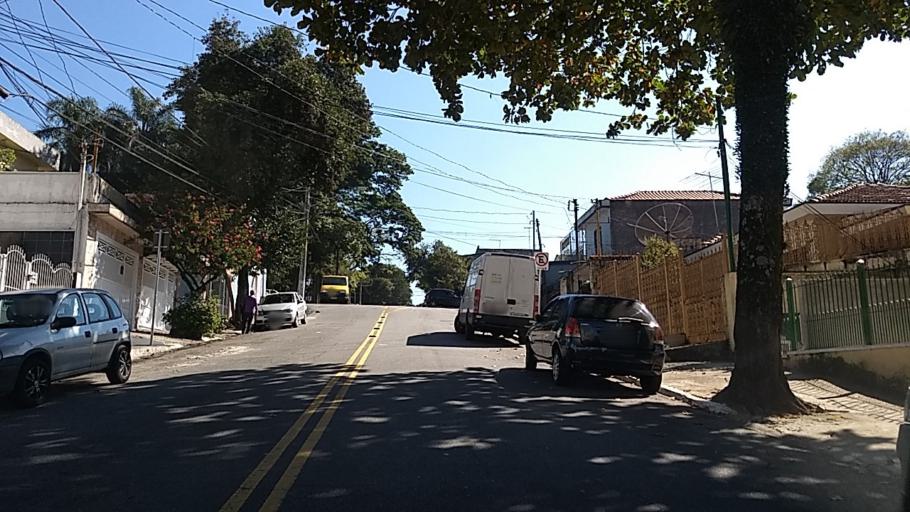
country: BR
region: Sao Paulo
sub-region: Guarulhos
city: Guarulhos
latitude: -23.4937
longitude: -46.5856
